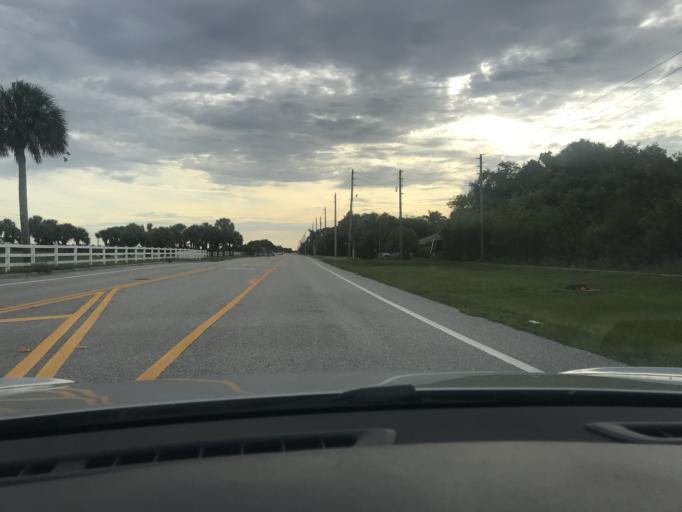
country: US
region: Florida
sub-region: Indian River County
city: West Vero Corridor
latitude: 27.6317
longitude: -80.4726
